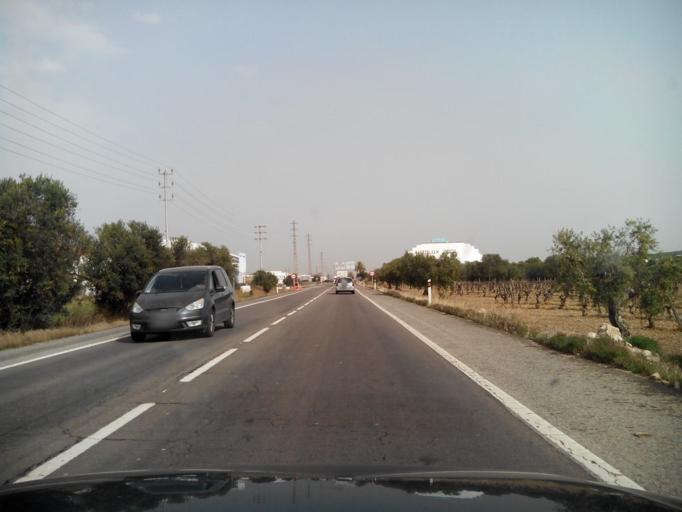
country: ES
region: Catalonia
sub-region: Provincia de Tarragona
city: El Vendrell
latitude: 41.2027
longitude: 1.5302
